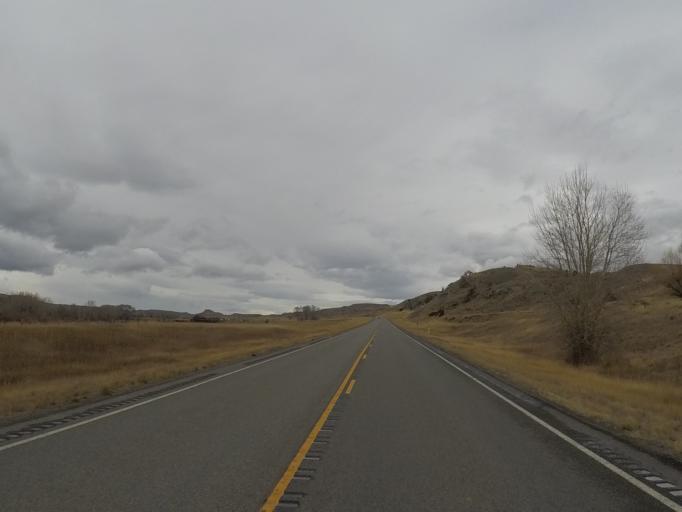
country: US
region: Montana
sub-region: Sweet Grass County
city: Big Timber
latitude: 45.9092
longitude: -109.9782
